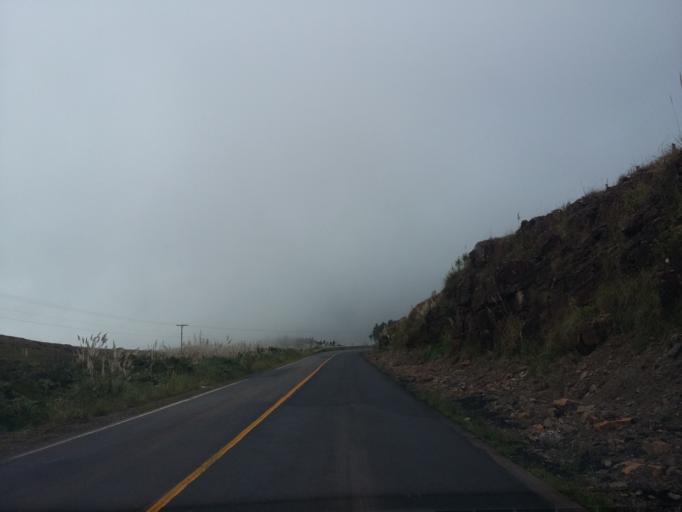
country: BR
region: Santa Catarina
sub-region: Lauro Muller
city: Lauro Muller
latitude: -28.3814
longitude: -49.5563
